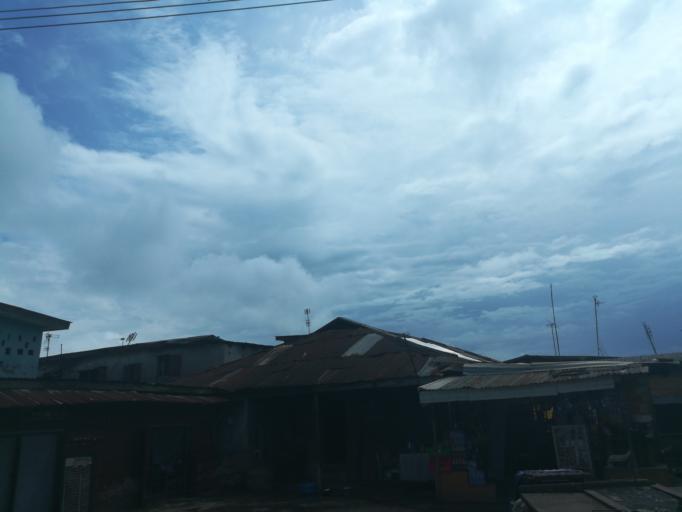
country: NG
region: Lagos
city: Agege
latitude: 6.6212
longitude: 3.3314
